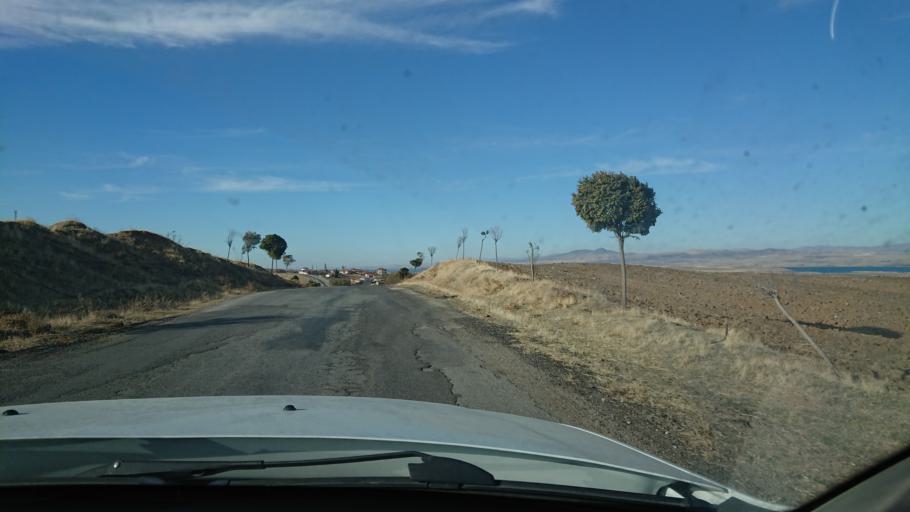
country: TR
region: Aksaray
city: Sariyahsi
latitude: 38.9735
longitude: 33.8593
